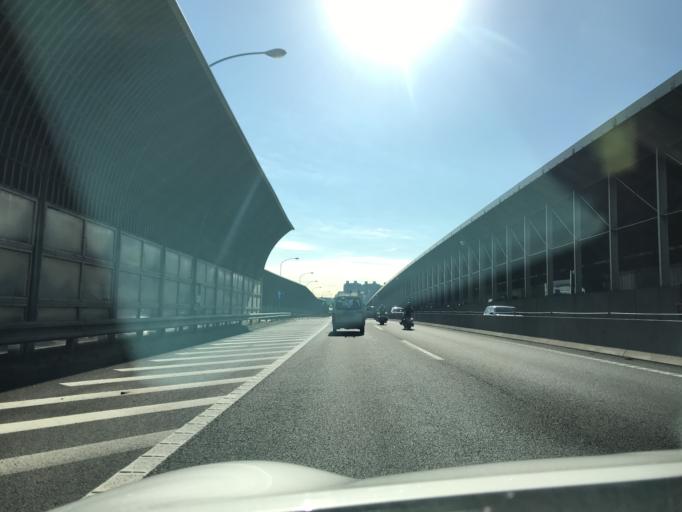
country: JP
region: Chiba
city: Chiba
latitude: 35.6365
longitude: 140.1206
